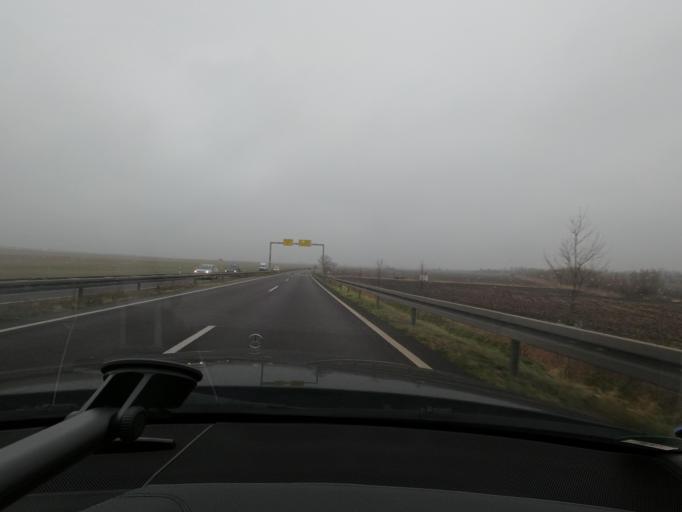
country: DE
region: Thuringia
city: Walschleben
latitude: 51.0727
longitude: 10.9279
